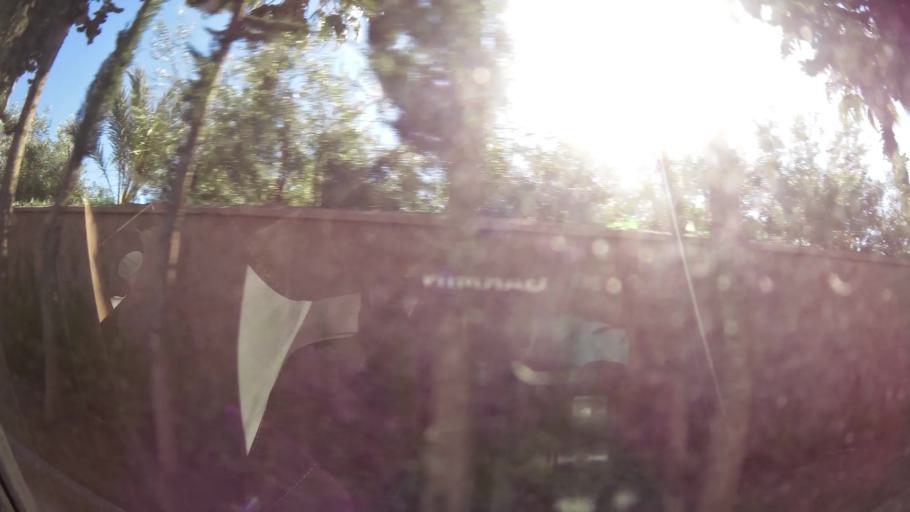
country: MA
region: Marrakech-Tensift-Al Haouz
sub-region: Marrakech
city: Marrakesh
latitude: 31.6653
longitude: -7.9404
